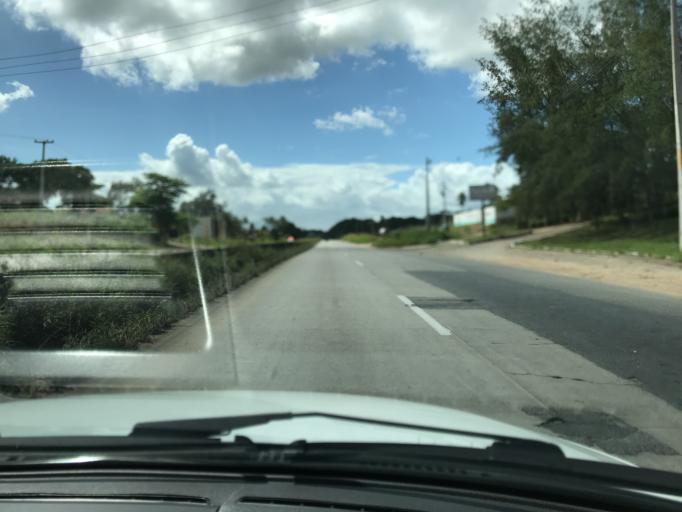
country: BR
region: Pernambuco
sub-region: Pombos
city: Pombos
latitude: -8.1405
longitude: -35.3795
